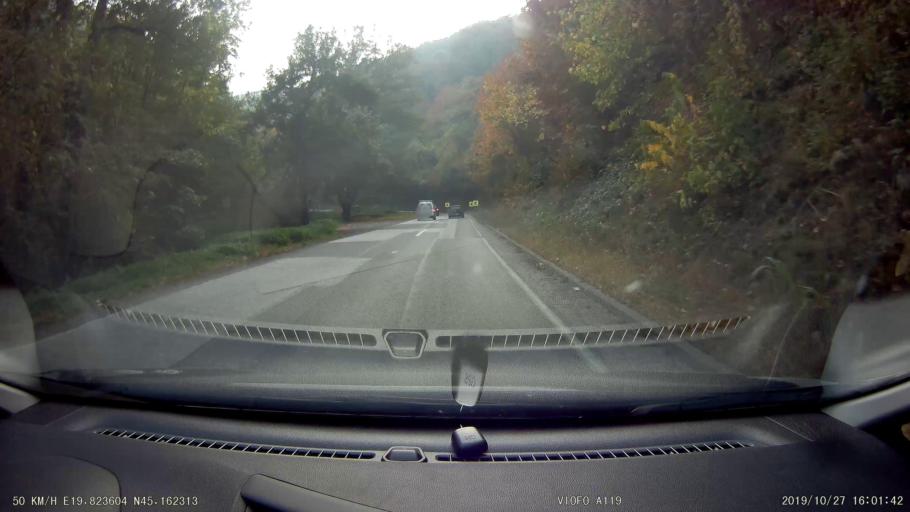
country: RS
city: Vrdnik
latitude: 45.1622
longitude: 19.8235
